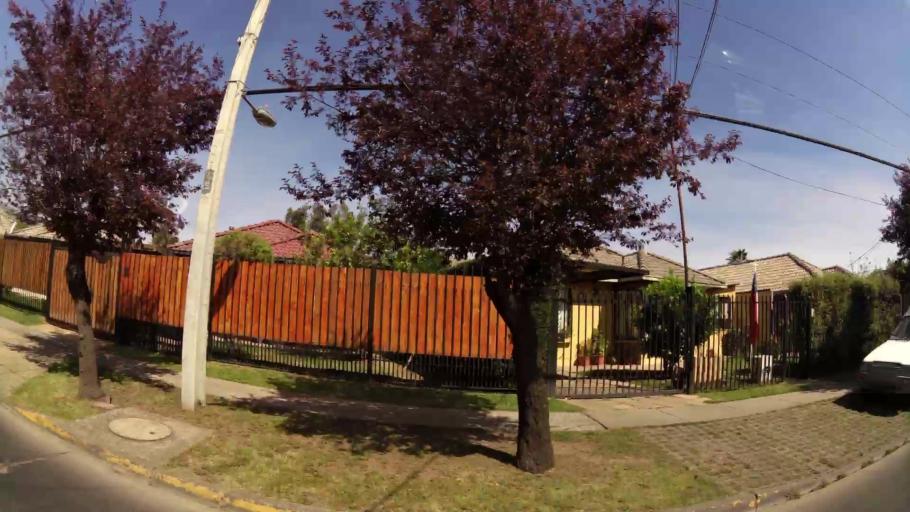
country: CL
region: Santiago Metropolitan
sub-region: Provincia de Santiago
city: Villa Presidente Frei, Nunoa, Santiago, Chile
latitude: -33.5354
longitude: -70.5639
